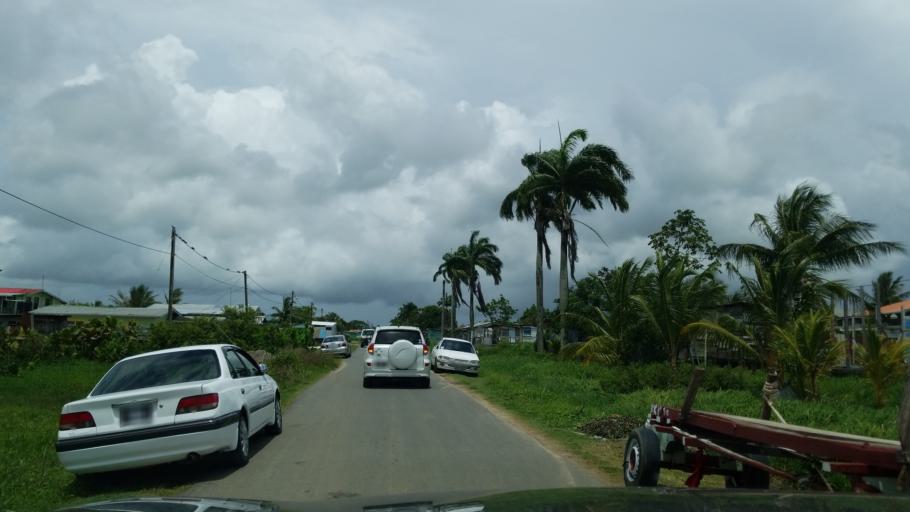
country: GY
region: Demerara-Mahaica
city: Georgetown
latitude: 6.7975
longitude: -58.1245
